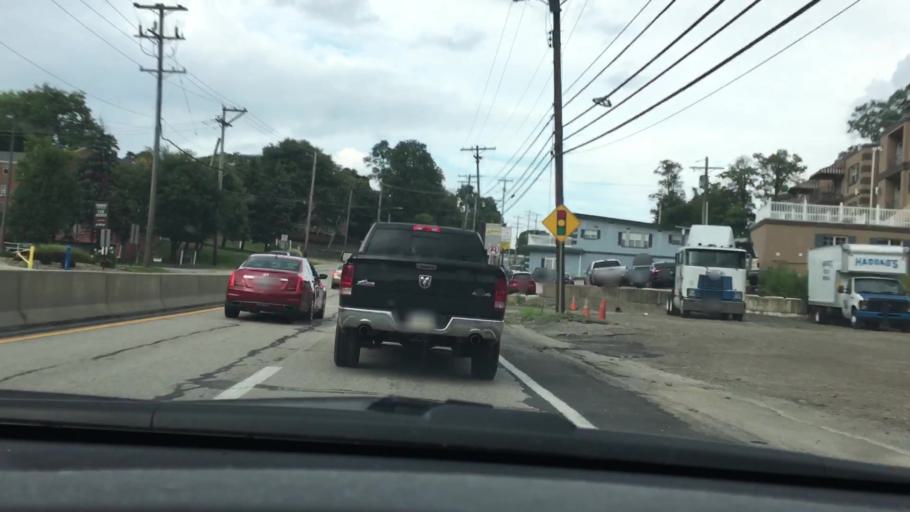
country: US
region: Pennsylvania
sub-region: Allegheny County
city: Pleasant Hills
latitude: 40.3389
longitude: -79.9682
